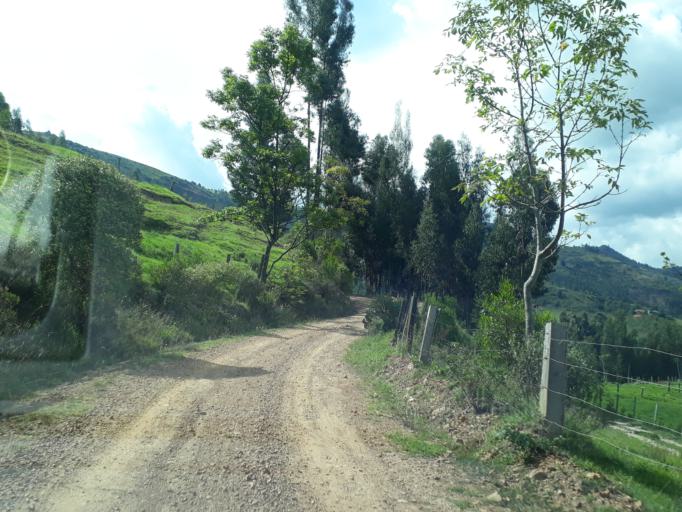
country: CO
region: Boyaca
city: Santa Rosa de Viterbo
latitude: 5.8533
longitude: -72.9670
